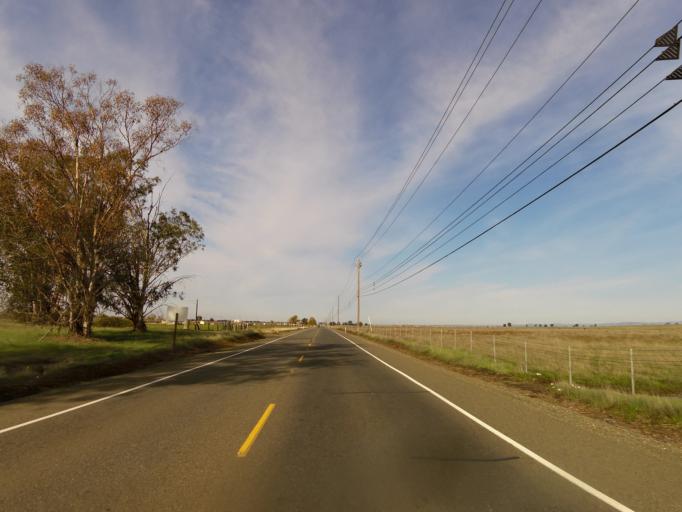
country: US
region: California
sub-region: Sacramento County
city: Wilton
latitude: 38.4884
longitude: -121.2422
